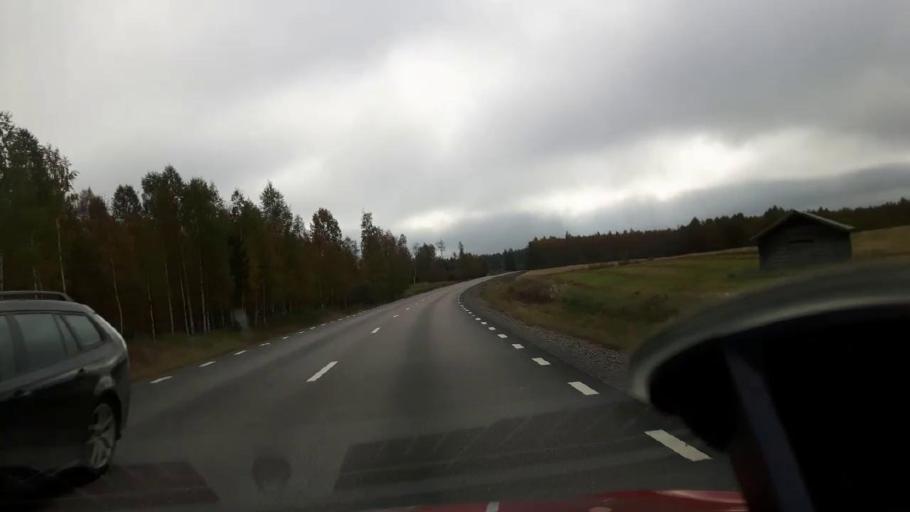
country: SE
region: Gaevleborg
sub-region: Ljusdals Kommun
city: Farila
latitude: 61.8633
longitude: 15.7386
